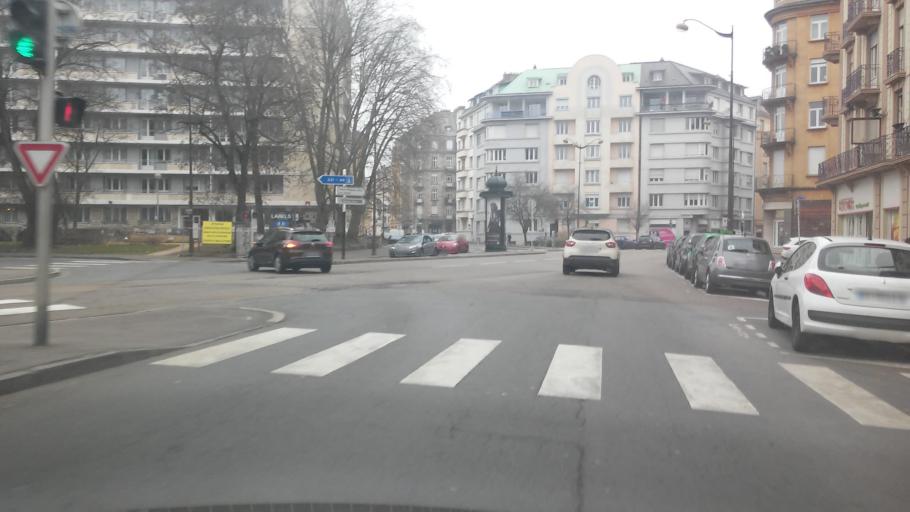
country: FR
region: Lorraine
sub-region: Departement de la Moselle
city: Metz
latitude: 49.1087
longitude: 6.1716
